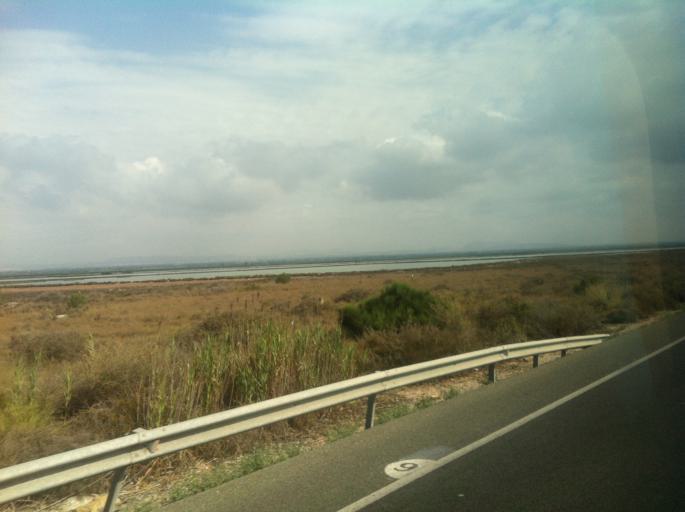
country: ES
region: Valencia
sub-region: Provincia de Alicante
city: Santa Pola
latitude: 38.1650
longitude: -0.6318
